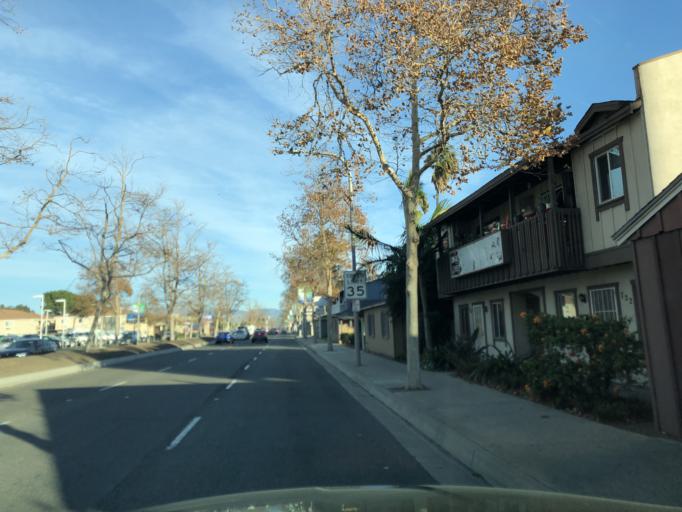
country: US
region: California
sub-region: Orange County
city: Santa Ana
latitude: 33.7599
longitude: -117.8595
